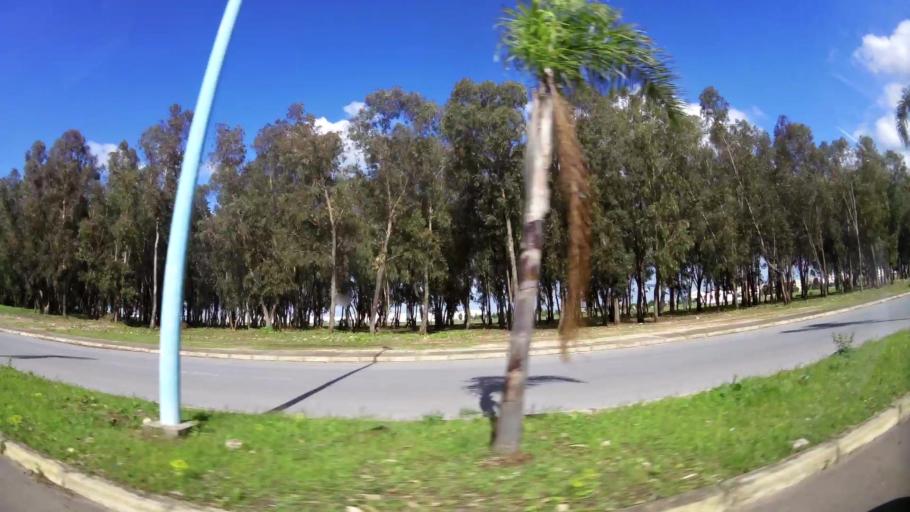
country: MA
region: Grand Casablanca
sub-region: Mediouna
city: Mediouna
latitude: 33.3906
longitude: -7.5518
